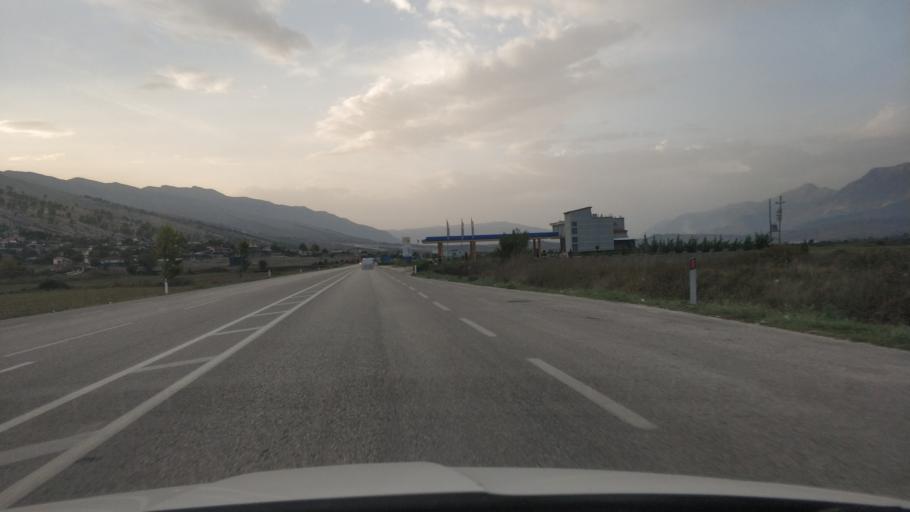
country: AL
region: Gjirokaster
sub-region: Rrethi i Gjirokastres
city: Dervician
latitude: 40.0140
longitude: 20.1993
